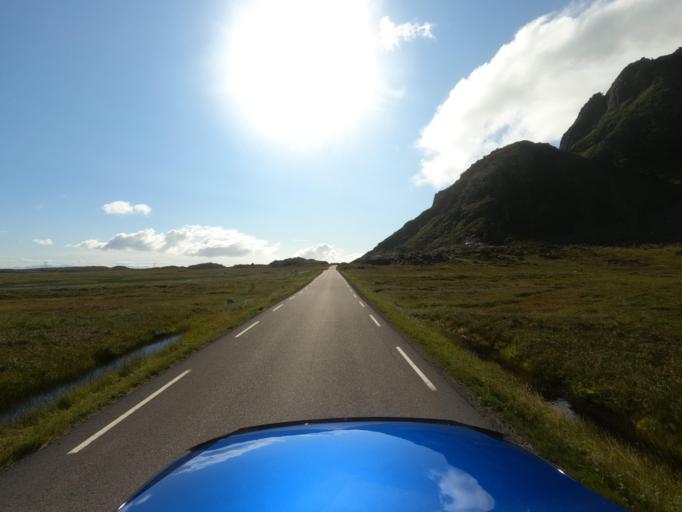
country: NO
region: Nordland
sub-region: Vestvagoy
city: Evjen
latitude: 68.2009
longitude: 14.0359
